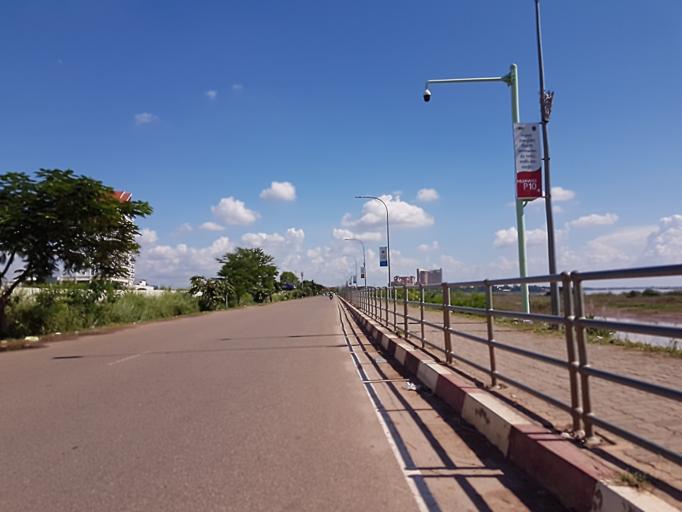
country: LA
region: Vientiane
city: Vientiane
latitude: 17.9559
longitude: 102.6124
